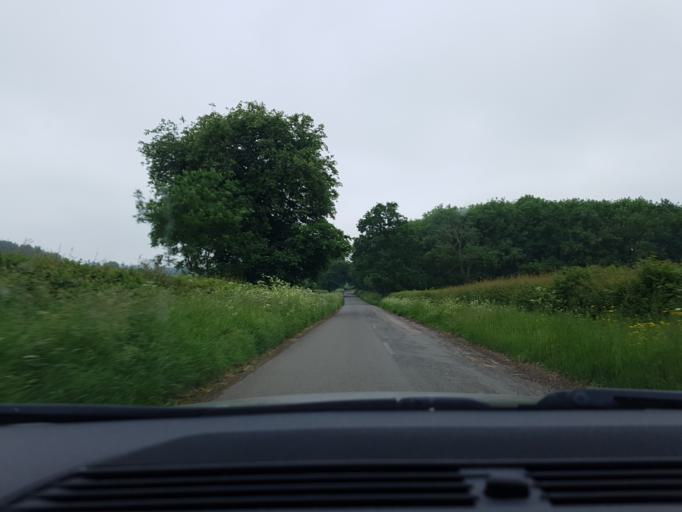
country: GB
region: England
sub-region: Buckinghamshire
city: Steeple Claydon
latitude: 51.9305
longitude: -0.9444
